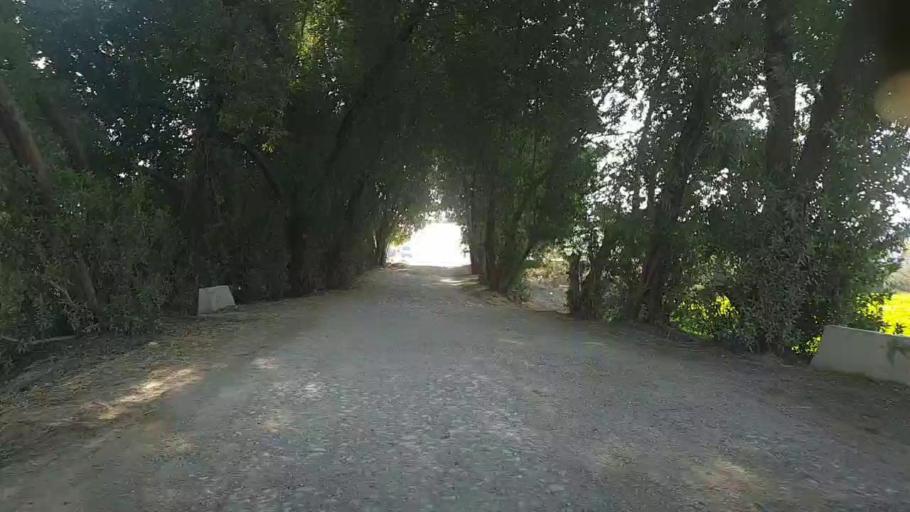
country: PK
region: Sindh
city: Khairpur
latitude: 28.0618
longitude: 69.6908
